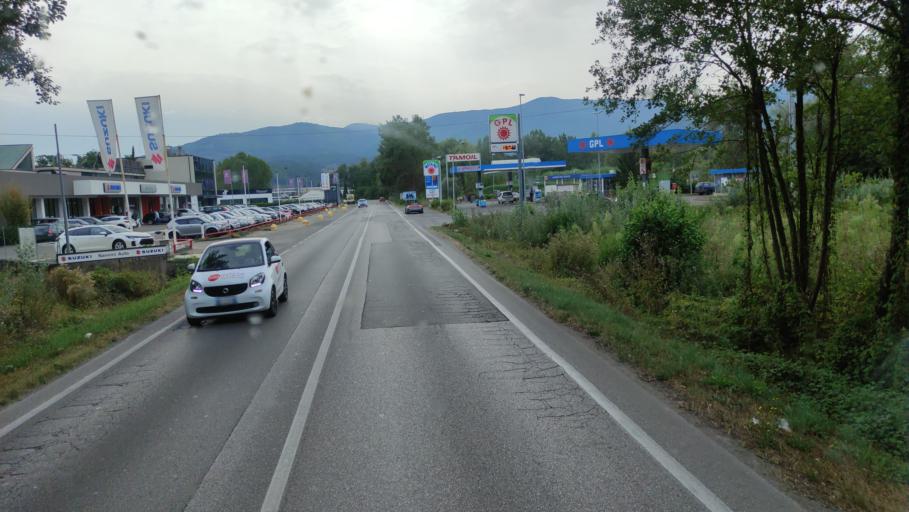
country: IT
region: Tuscany
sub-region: Provincia di Lucca
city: Lucca
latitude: 43.8183
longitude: 10.4929
